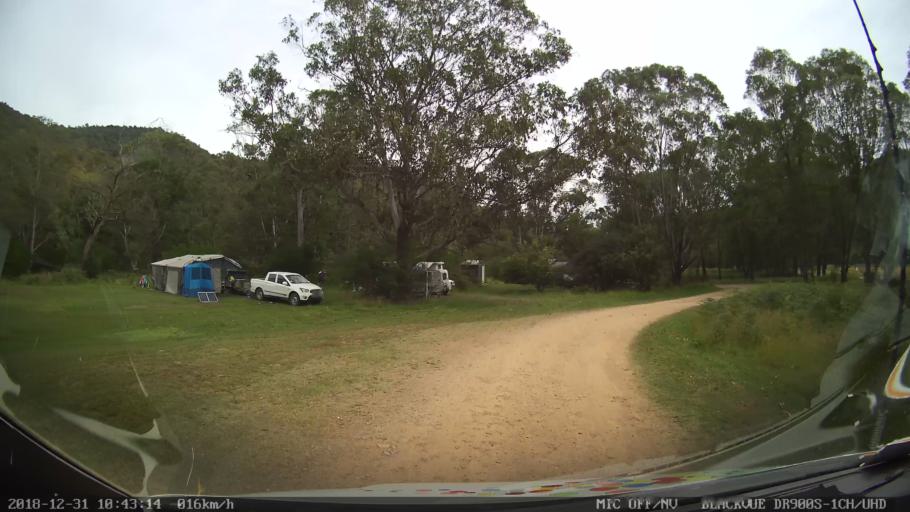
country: AU
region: New South Wales
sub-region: Snowy River
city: Jindabyne
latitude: -36.3809
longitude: 148.1788
